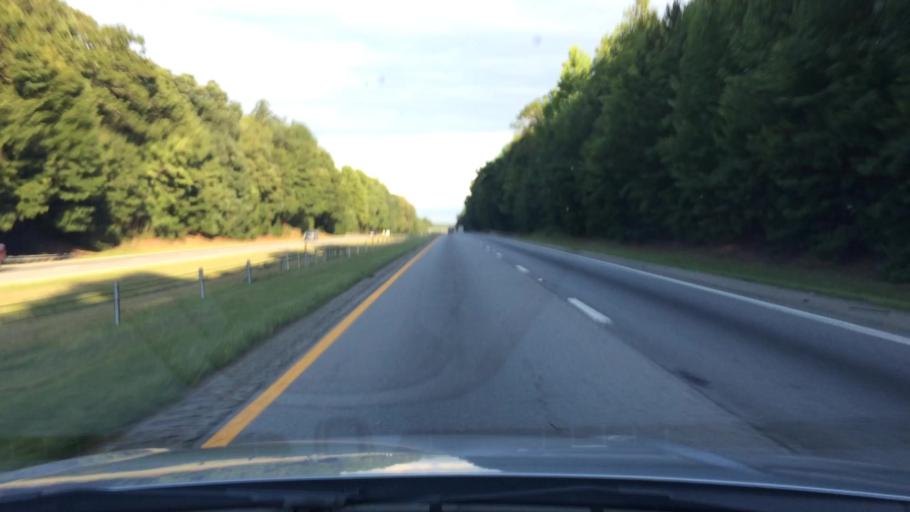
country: US
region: South Carolina
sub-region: Lexington County
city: Chapin
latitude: 34.1981
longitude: -81.3598
